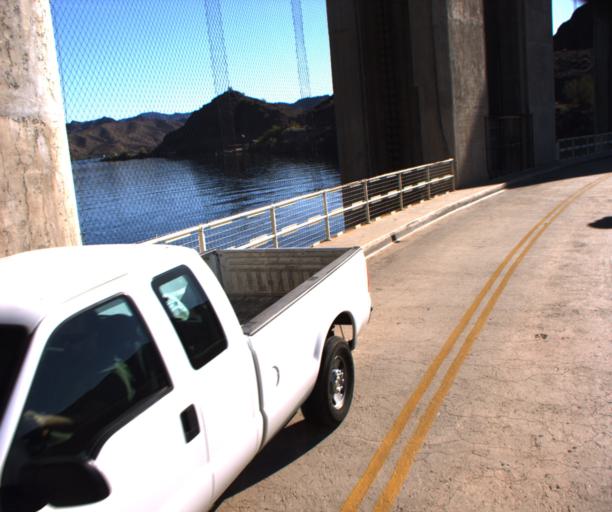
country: US
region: Arizona
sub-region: La Paz County
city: Cienega Springs
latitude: 34.2966
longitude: -114.1397
